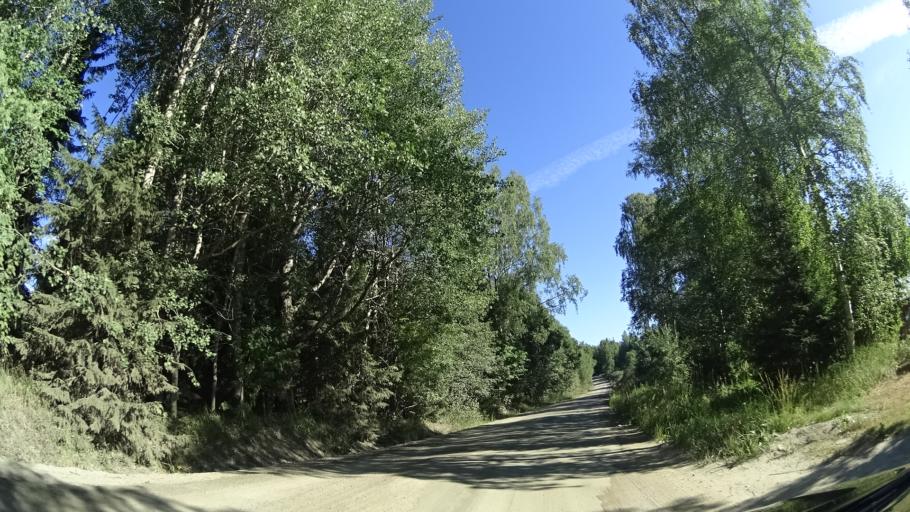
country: FI
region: Central Finland
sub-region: Jyvaeskylae
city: Petaejaevesi
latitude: 62.2849
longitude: 25.3227
